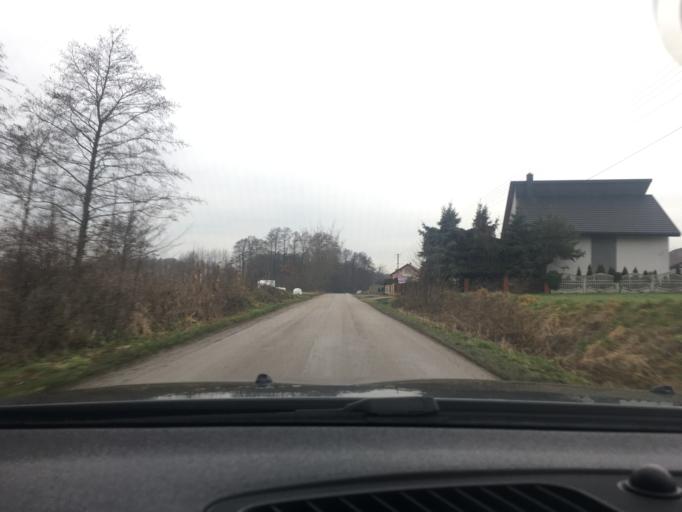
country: PL
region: Swietokrzyskie
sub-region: Powiat jedrzejowski
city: Imielno
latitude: 50.6421
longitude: 20.4026
